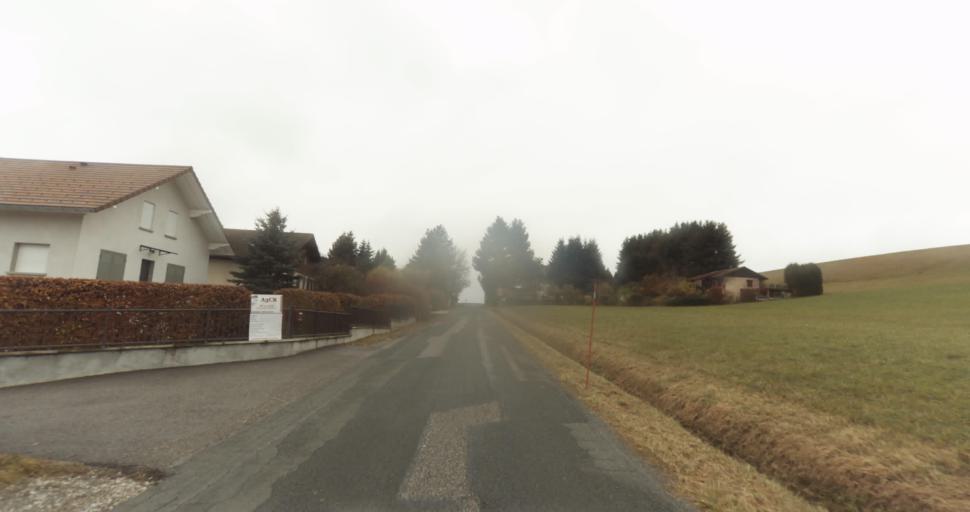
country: FR
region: Rhone-Alpes
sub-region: Departement de la Haute-Savoie
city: Evires
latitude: 46.0393
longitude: 6.2294
